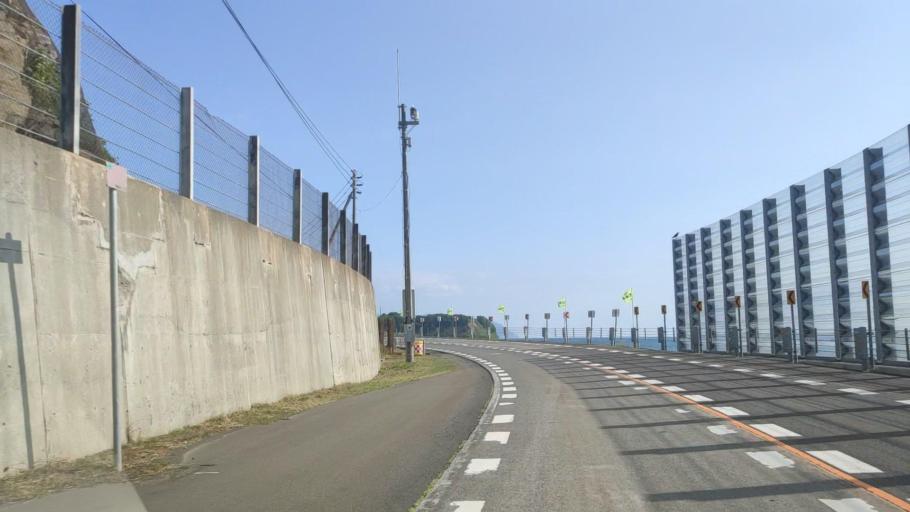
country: JP
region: Hokkaido
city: Rumoi
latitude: 43.6544
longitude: 141.3504
